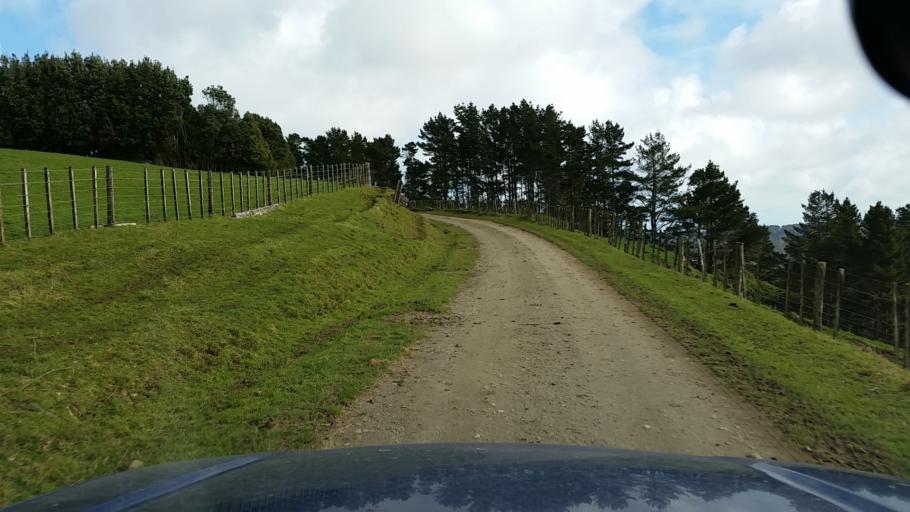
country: NZ
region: Taranaki
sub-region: South Taranaki District
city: Patea
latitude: -39.6601
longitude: 174.5673
